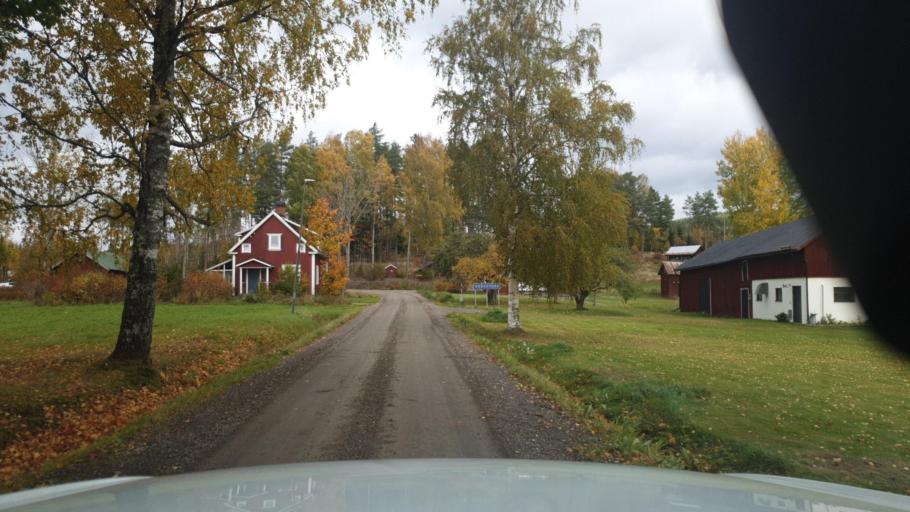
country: SE
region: Vaermland
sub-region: Sunne Kommun
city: Sunne
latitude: 59.8151
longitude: 13.0561
